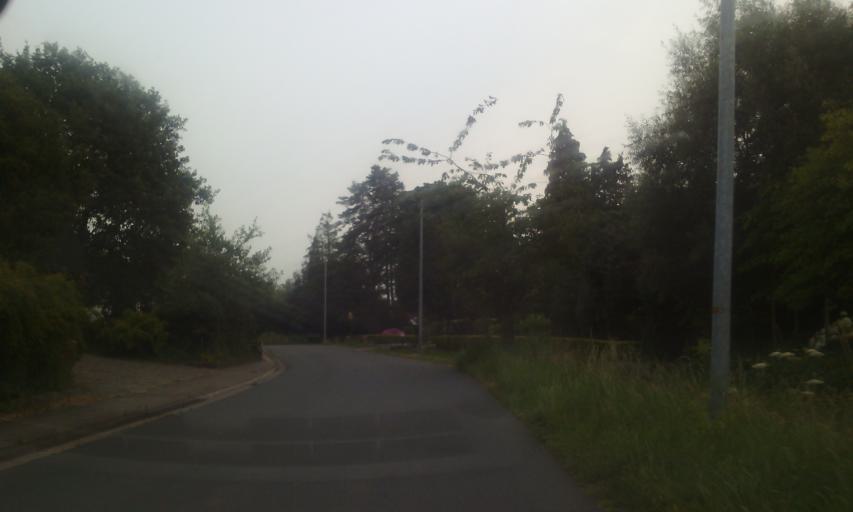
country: BE
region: Flanders
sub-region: Provincie Oost-Vlaanderen
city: Lede
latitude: 50.9884
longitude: 4.0330
